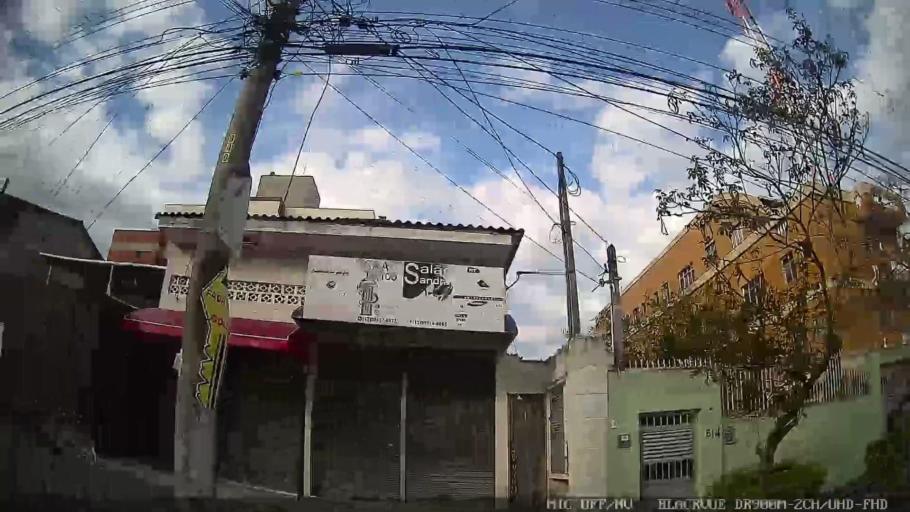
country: BR
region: Sao Paulo
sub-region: Guaruja
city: Guaruja
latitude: -23.9826
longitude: -46.2377
